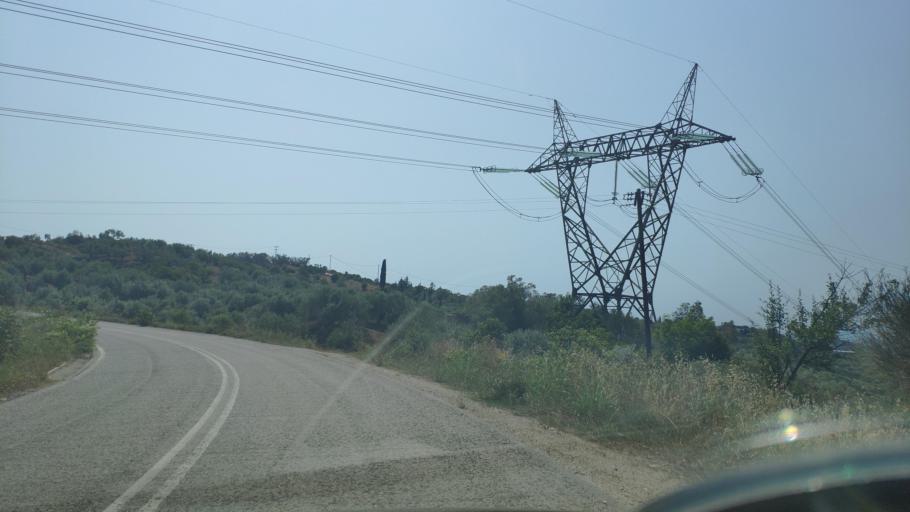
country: GR
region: Epirus
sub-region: Nomos Artas
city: Peta
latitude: 39.1702
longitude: 21.0558
